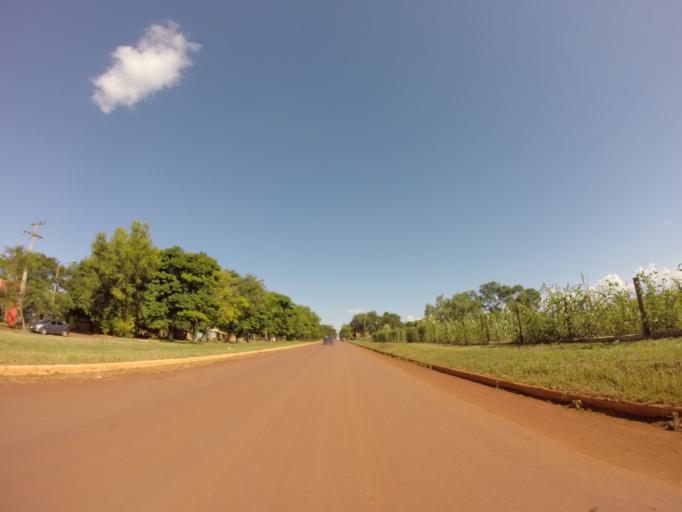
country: PY
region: Alto Parana
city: Ciudad del Este
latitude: -25.3761
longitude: -54.6552
